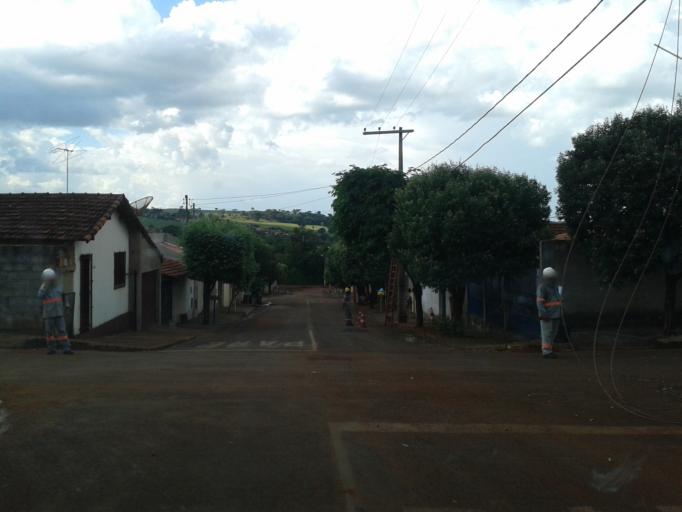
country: BR
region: Minas Gerais
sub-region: Capinopolis
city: Capinopolis
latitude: -18.6852
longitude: -49.5806
